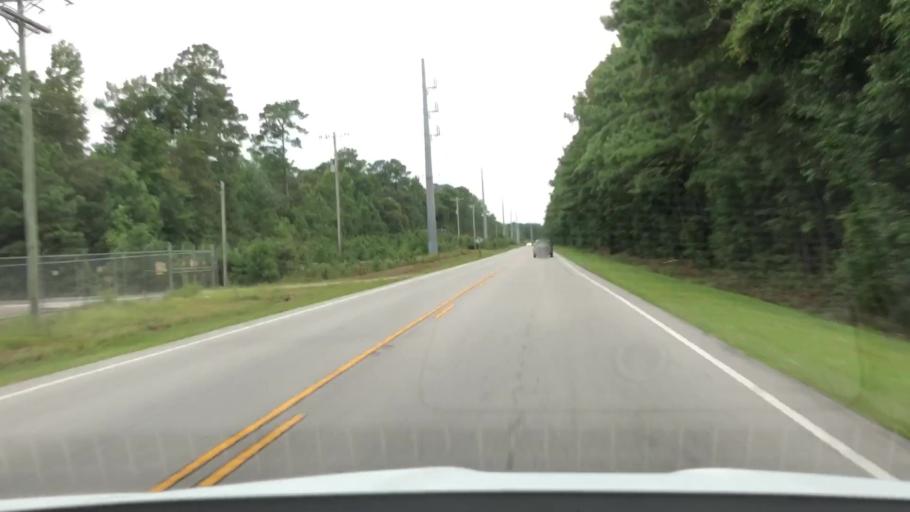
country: US
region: North Carolina
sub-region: Carteret County
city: Cape Carteret
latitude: 34.7415
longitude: -77.0866
